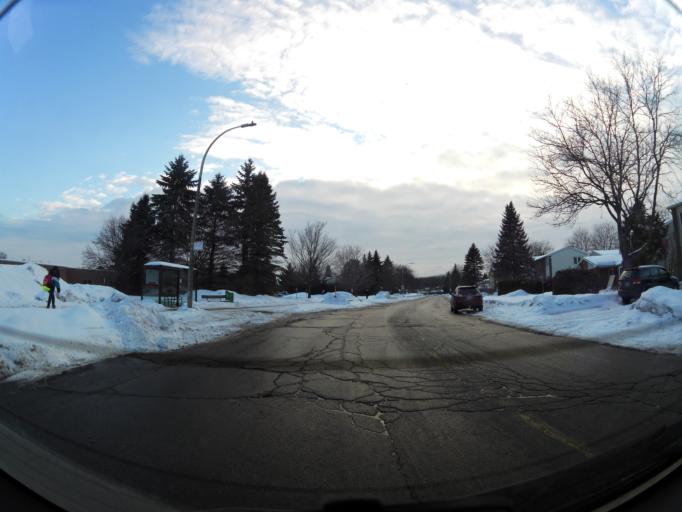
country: CA
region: Ontario
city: Ottawa
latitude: 45.4527
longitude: -75.5406
